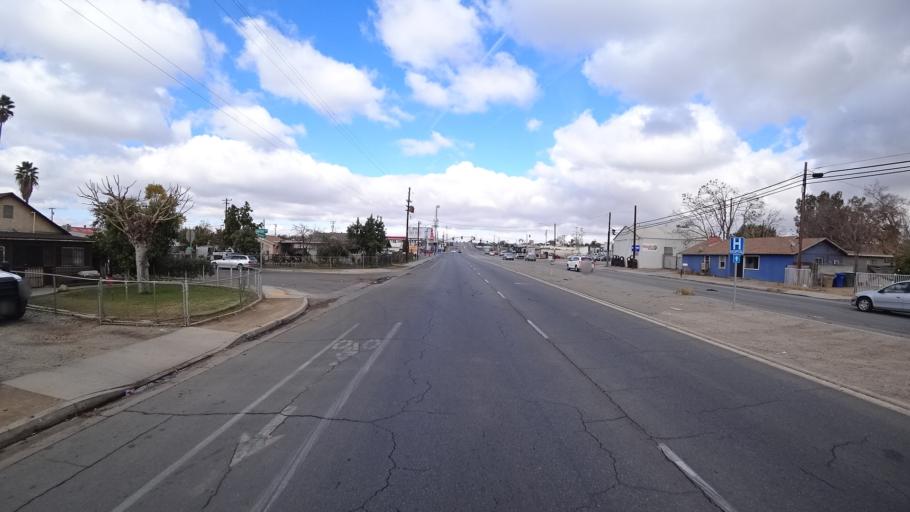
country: US
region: California
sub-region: Kern County
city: Bakersfield
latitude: 35.3670
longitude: -118.9676
